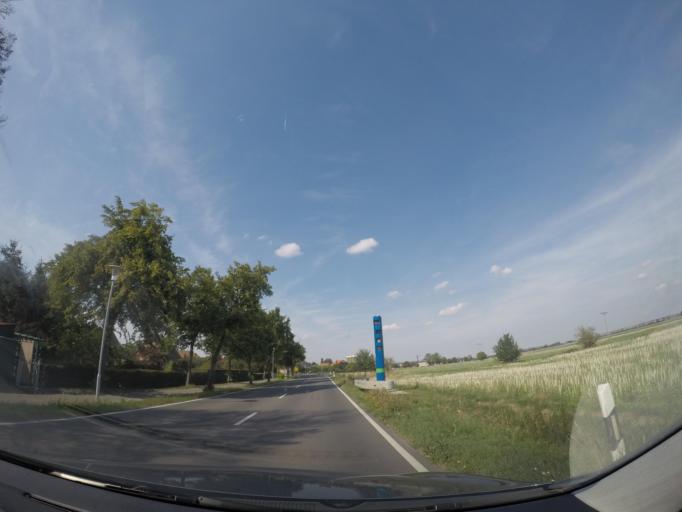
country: DE
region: Saxony-Anhalt
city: Wasserleben
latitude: 51.8879
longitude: 10.7685
